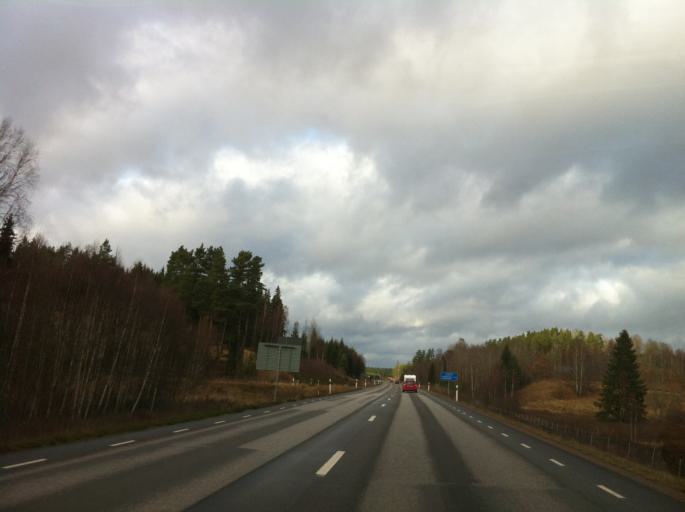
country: SE
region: Kalmar
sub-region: Vimmerby Kommun
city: Vimmerby
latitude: 57.5936
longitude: 15.8481
